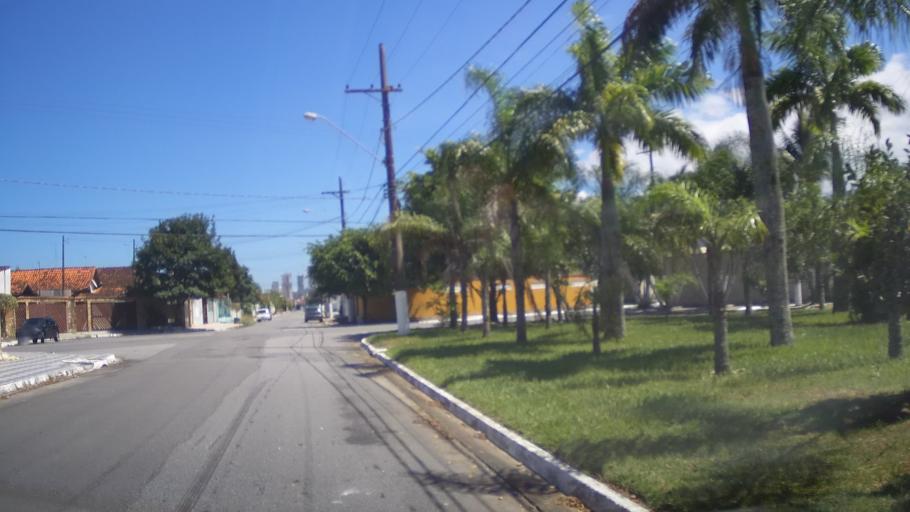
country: BR
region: Sao Paulo
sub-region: Mongagua
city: Mongagua
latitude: -24.0425
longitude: -46.5167
